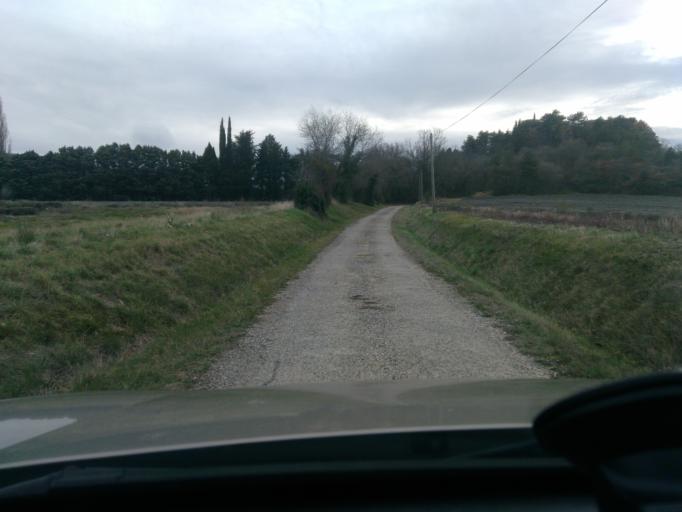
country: FR
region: Rhone-Alpes
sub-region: Departement de la Drome
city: Montboucher-sur-Jabron
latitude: 44.5453
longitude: 4.8507
